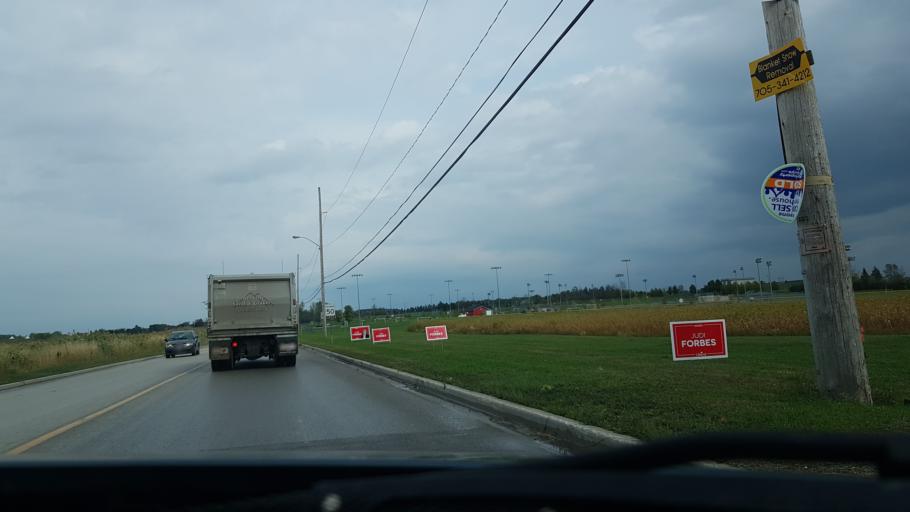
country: CA
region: Ontario
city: Omemee
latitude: 44.3535
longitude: -78.7702
